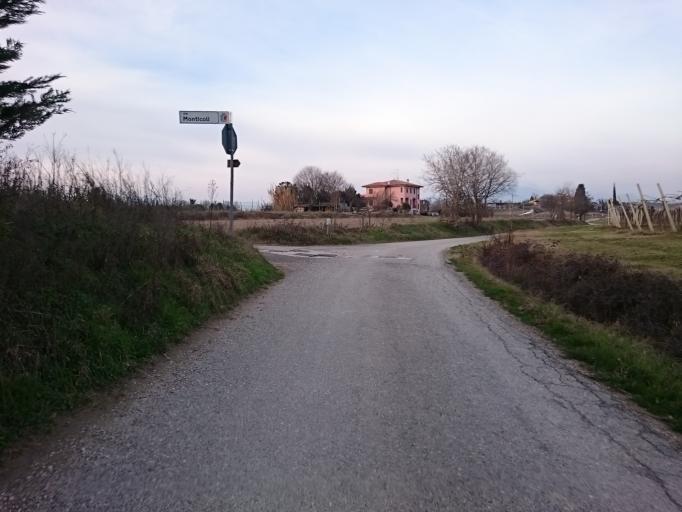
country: IT
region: Veneto
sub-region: Provincia di Verona
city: Cola
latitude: 45.4570
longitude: 10.7343
